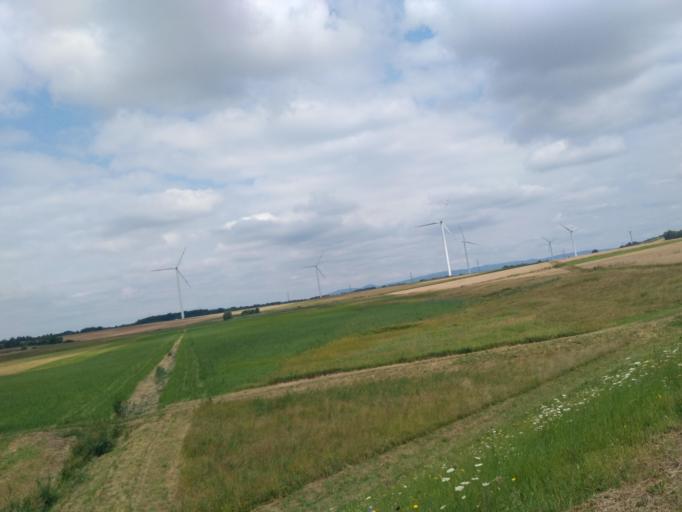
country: PL
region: Subcarpathian Voivodeship
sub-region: Powiat krosnienski
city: Rymanow
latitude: 49.5961
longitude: 21.8460
